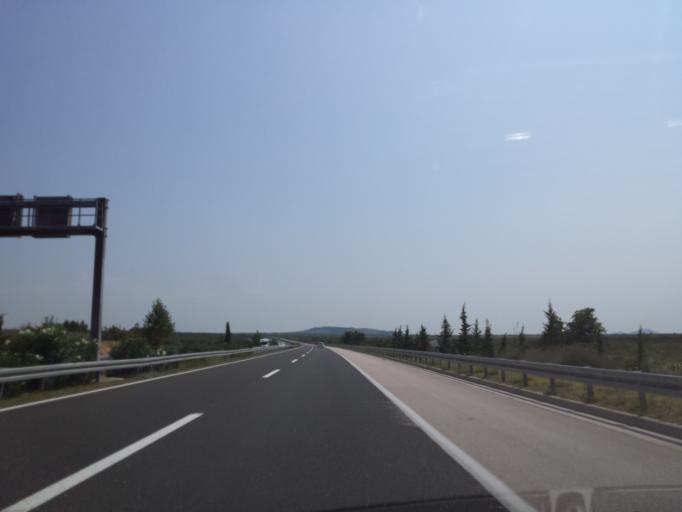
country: HR
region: Zadarska
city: Galovac
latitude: 44.1039
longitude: 15.4618
